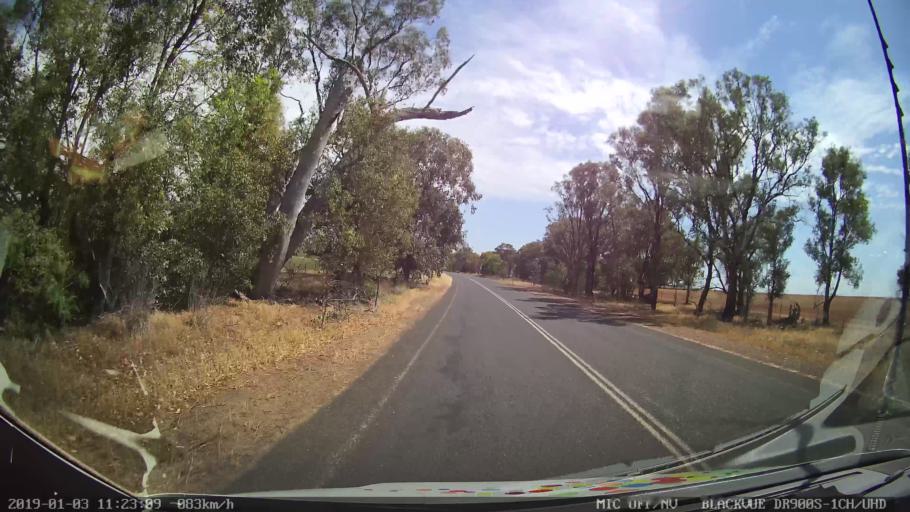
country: AU
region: New South Wales
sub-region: Weddin
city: Grenfell
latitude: -34.0666
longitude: 148.2440
